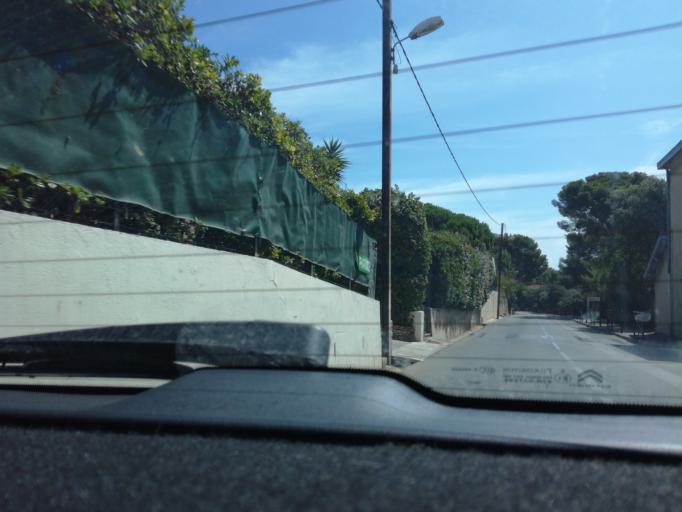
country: FR
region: Provence-Alpes-Cote d'Azur
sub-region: Departement du Var
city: Hyeres
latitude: 43.0376
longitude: 6.1382
